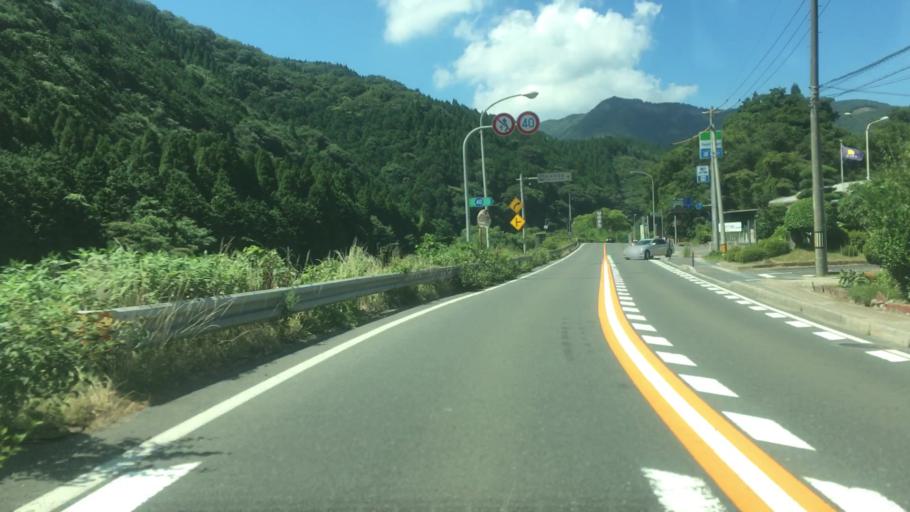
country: JP
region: Tottori
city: Tottori
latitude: 35.2729
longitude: 134.2241
